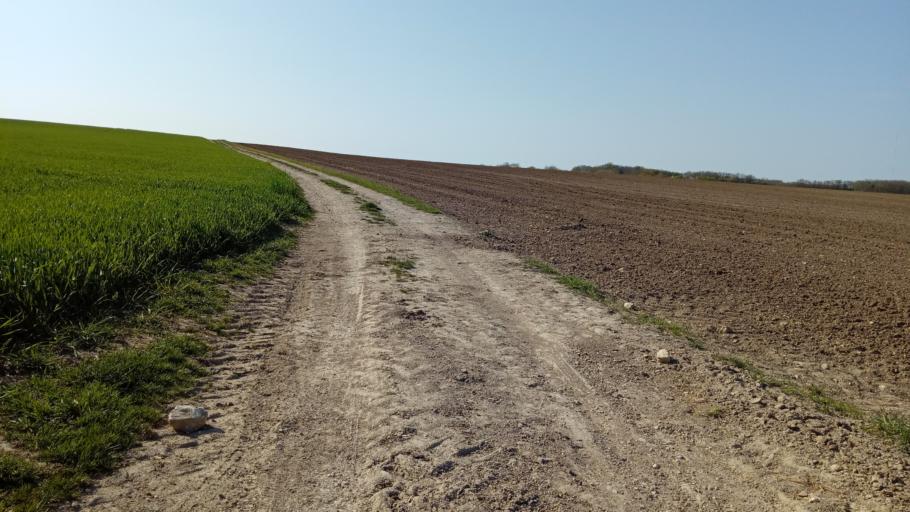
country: FR
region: Poitou-Charentes
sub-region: Departement de la Charente-Maritime
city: Verines
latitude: 46.1580
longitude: -0.9252
